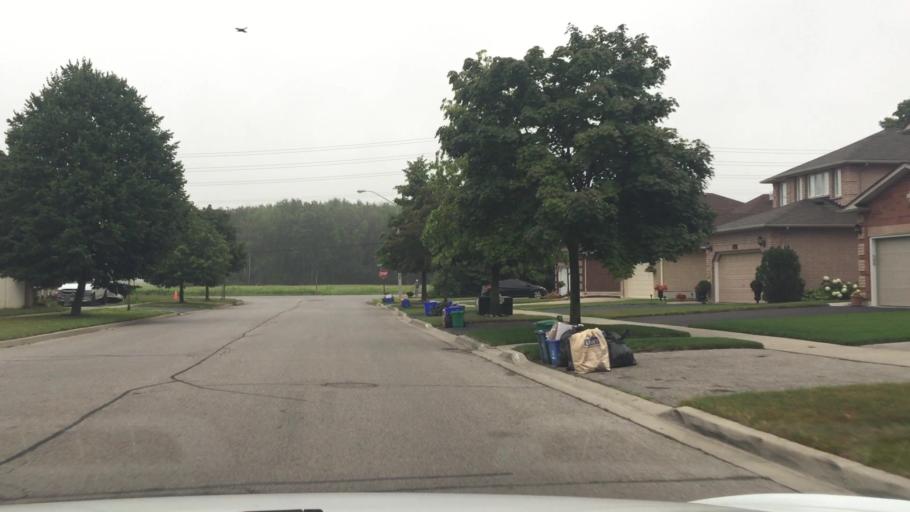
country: CA
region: Ontario
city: Oshawa
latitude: 43.9092
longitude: -78.7780
